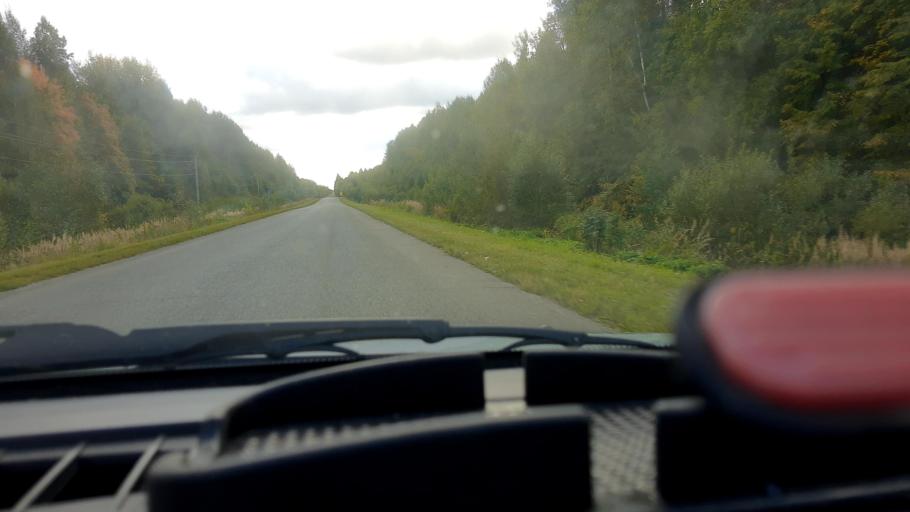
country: RU
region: Mariy-El
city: Kilemary
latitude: 56.9132
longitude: 46.7260
